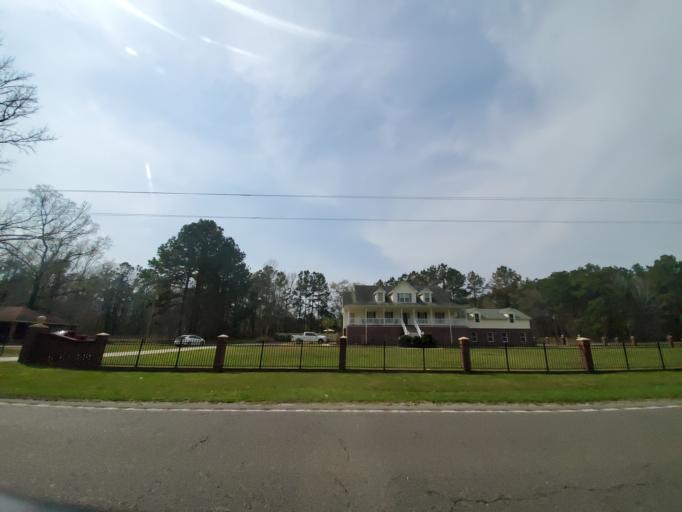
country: US
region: South Carolina
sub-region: Dorchester County
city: Ridgeville
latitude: 32.9767
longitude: -80.3065
